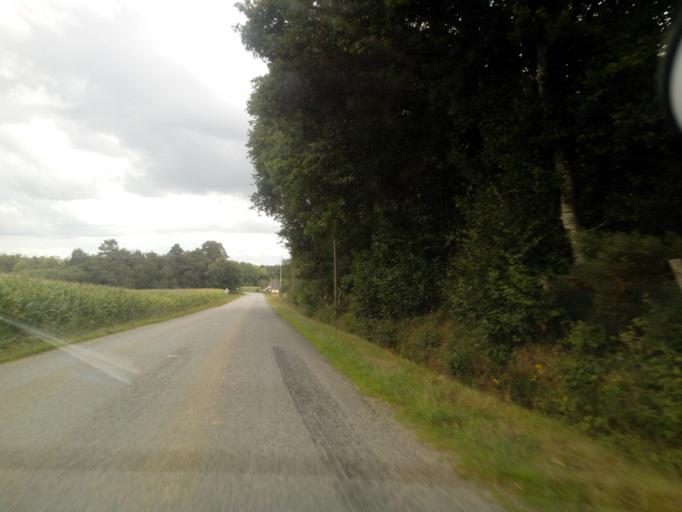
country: FR
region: Brittany
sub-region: Departement du Morbihan
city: Mauron
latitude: 48.0989
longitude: -2.3519
